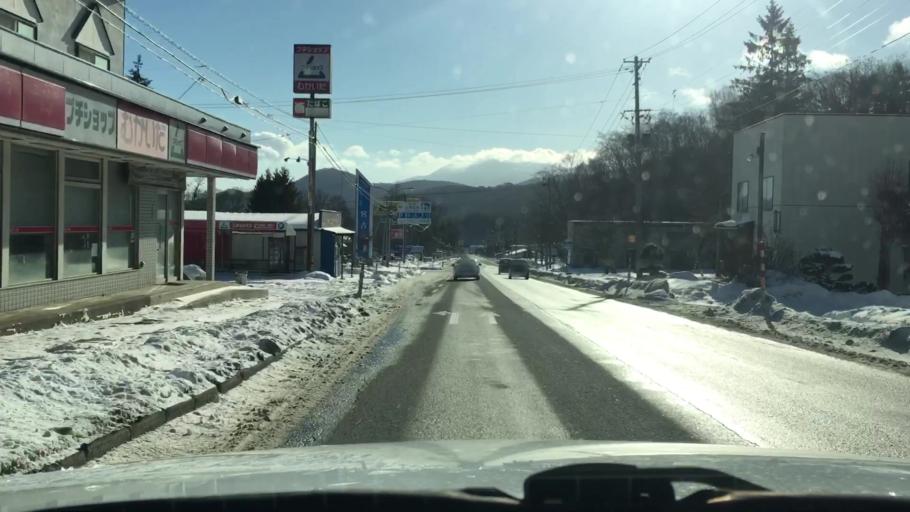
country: JP
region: Iwate
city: Morioka-shi
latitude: 39.6518
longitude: 141.3521
